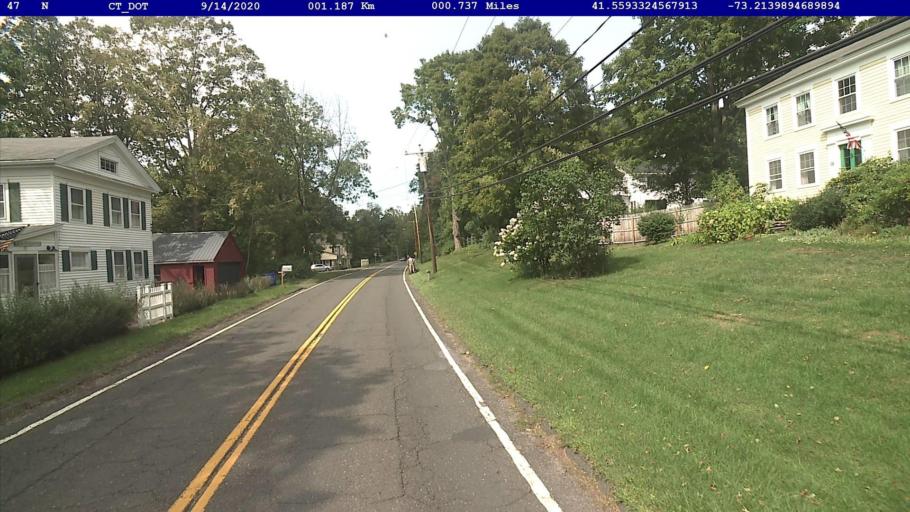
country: US
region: Connecticut
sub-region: Litchfield County
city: Woodbury
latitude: 41.5593
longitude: -73.2140
